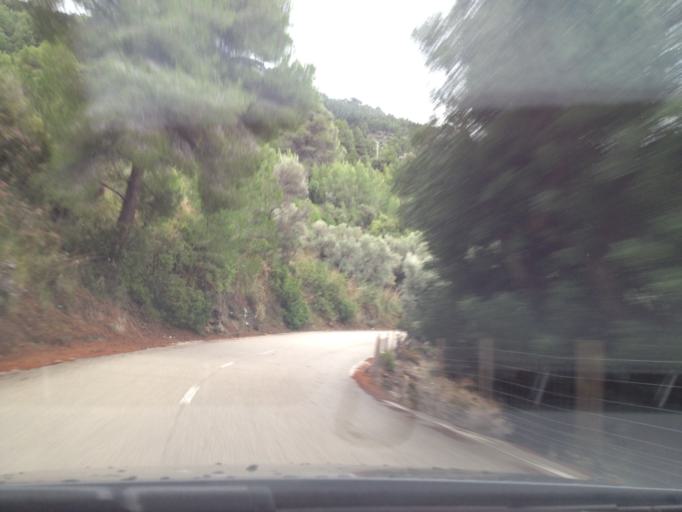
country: ES
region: Balearic Islands
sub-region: Illes Balears
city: Deia
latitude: 39.7695
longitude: 2.6634
